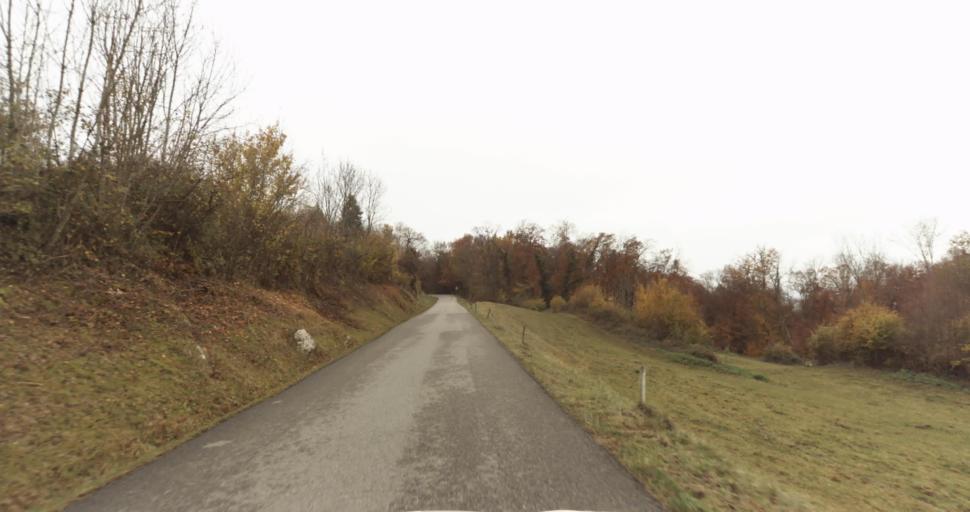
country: FR
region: Rhone-Alpes
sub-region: Departement de la Haute-Savoie
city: Cusy
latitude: 45.7503
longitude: 6.0137
